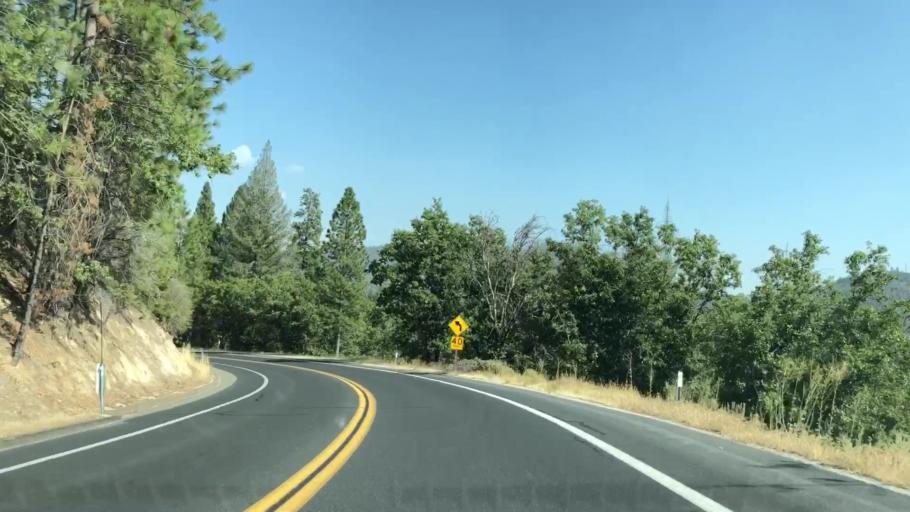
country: US
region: California
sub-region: Mariposa County
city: Midpines
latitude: 37.8160
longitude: -119.9494
